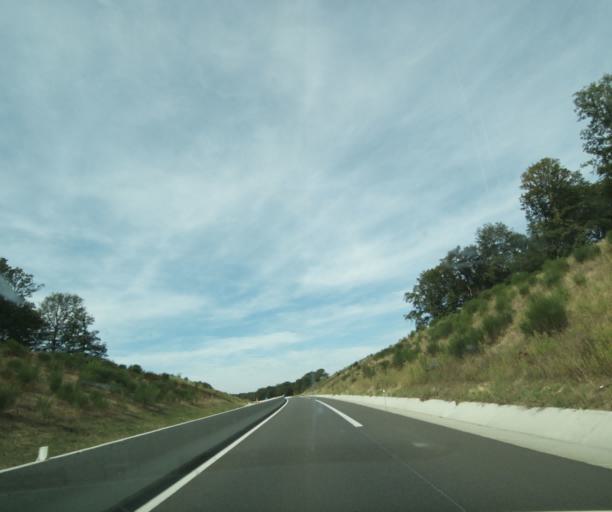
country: FR
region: Auvergne
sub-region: Departement de l'Allier
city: Vendat
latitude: 46.1352
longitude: 3.3586
